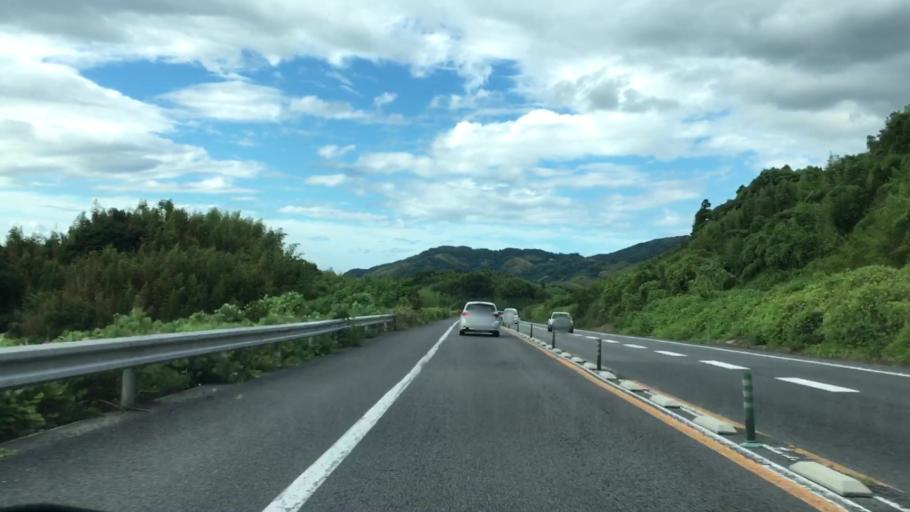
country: JP
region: Saga Prefecture
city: Karatsu
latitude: 33.4343
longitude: 130.0482
